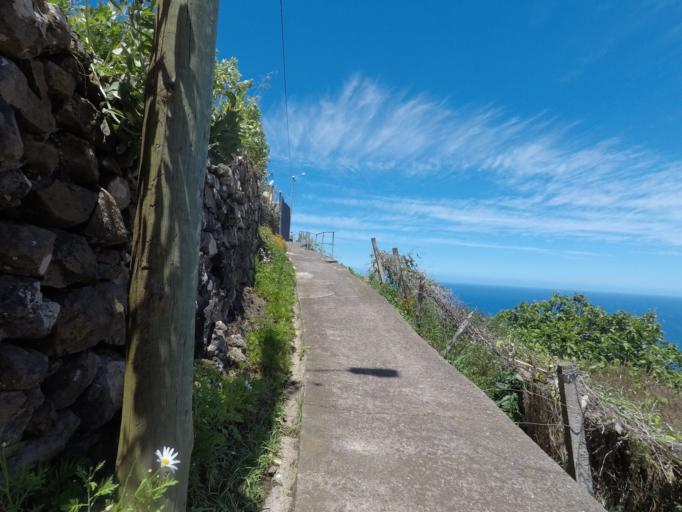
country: PT
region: Madeira
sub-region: Sao Vicente
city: Sao Vicente
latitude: 32.8256
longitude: -16.9791
